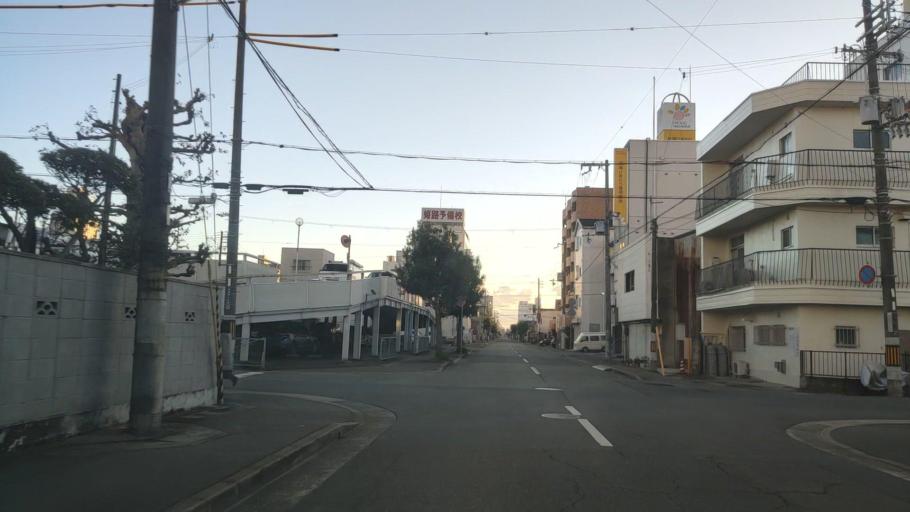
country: JP
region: Hyogo
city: Himeji
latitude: 34.8257
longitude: 134.6855
